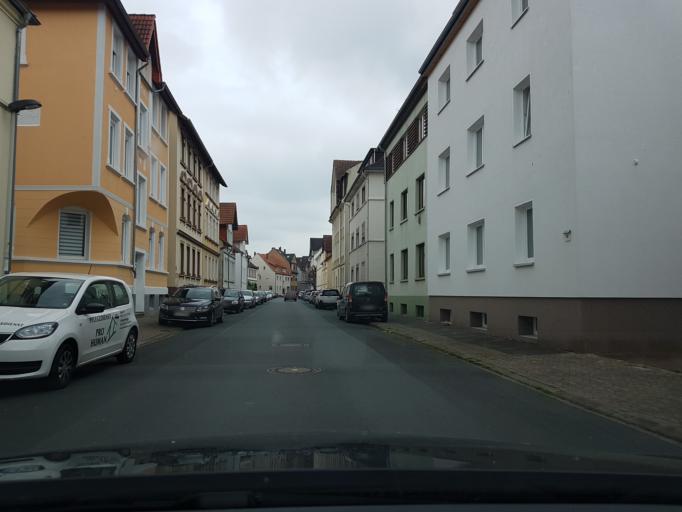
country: DE
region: Lower Saxony
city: Hameln
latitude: 52.1064
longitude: 9.3725
